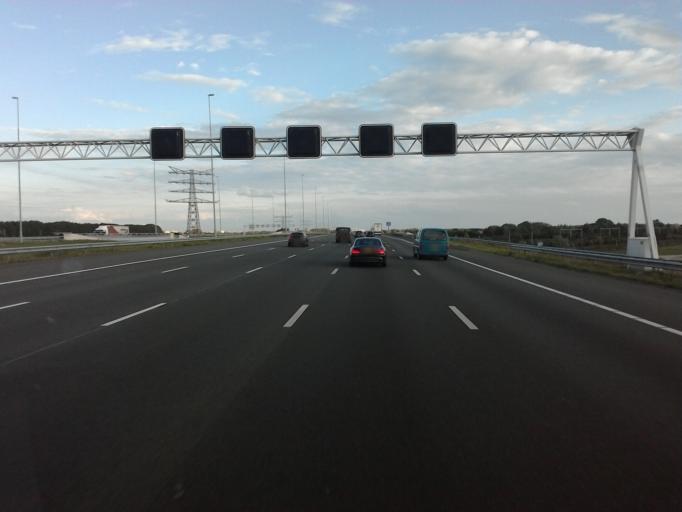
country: NL
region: Utrecht
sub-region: Stichtse Vecht
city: Breukelen
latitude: 52.1621
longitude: 4.9894
